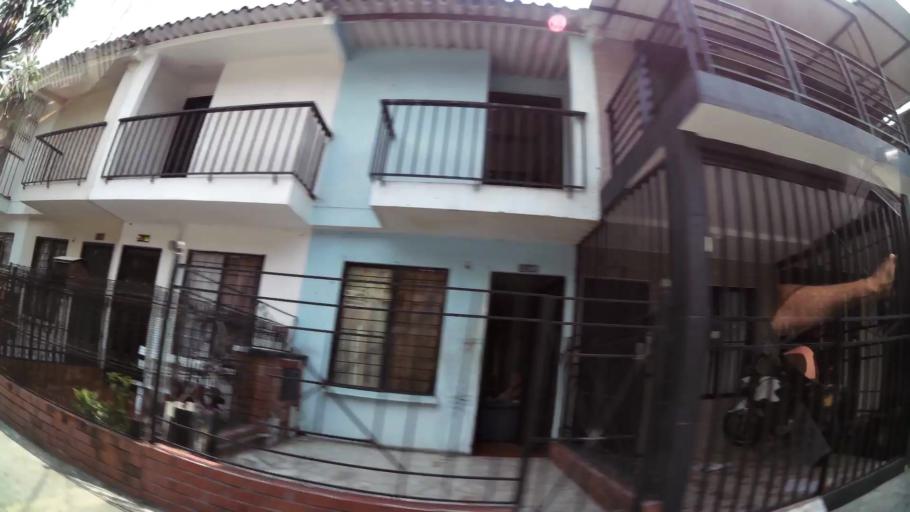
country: CO
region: Valle del Cauca
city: Cali
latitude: 3.4918
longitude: -76.5037
